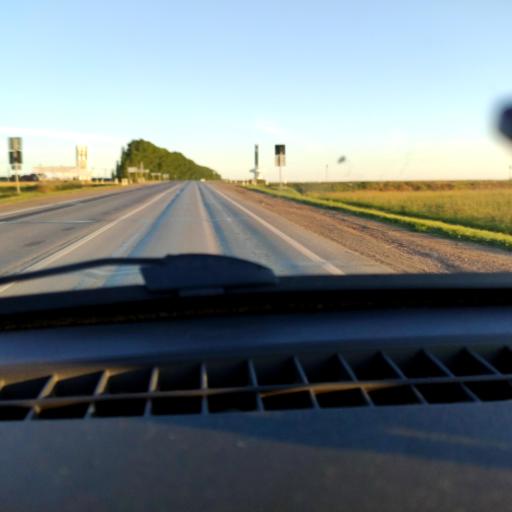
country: RU
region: Bashkortostan
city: Kabakovo
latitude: 54.4680
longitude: 55.9509
